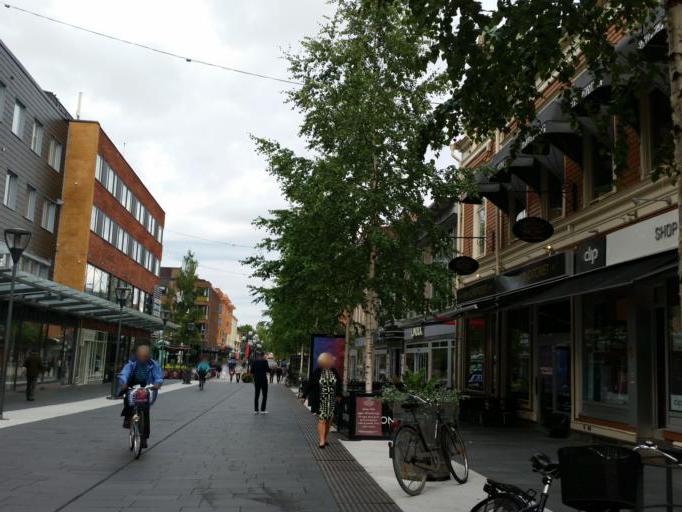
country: SE
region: Vaesterbotten
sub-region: Umea Kommun
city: Umea
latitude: 63.8261
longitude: 20.2619
